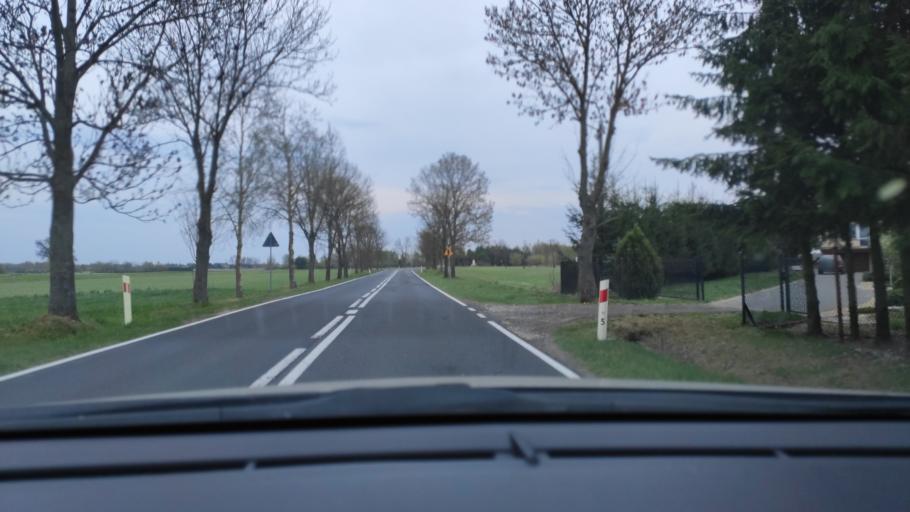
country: PL
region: Masovian Voivodeship
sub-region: Powiat zwolenski
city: Zwolen
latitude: 51.3817
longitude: 21.5599
